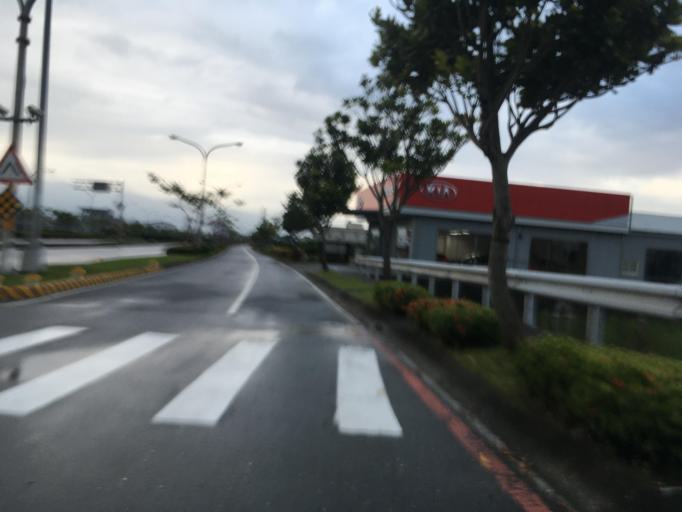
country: TW
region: Taiwan
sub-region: Yilan
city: Yilan
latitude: 24.7258
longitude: 121.7724
